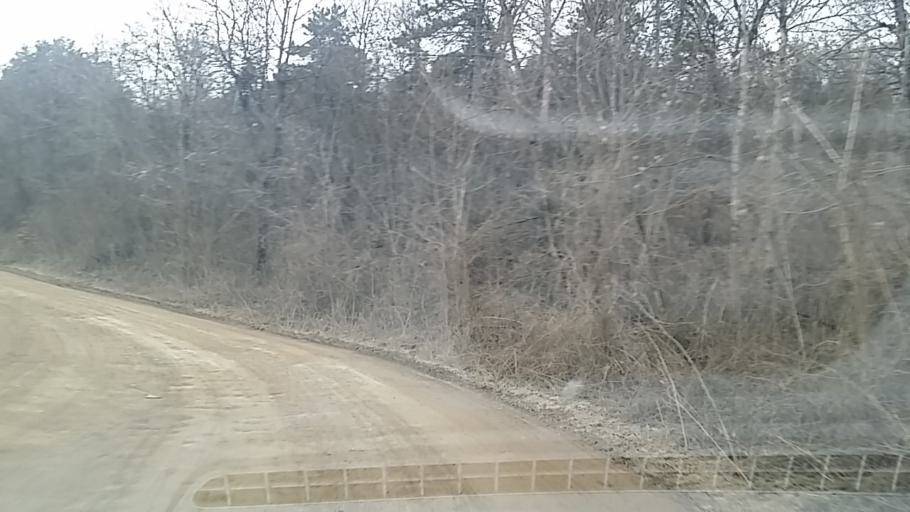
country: HU
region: Borsod-Abauj-Zemplen
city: Rudabanya
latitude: 48.3860
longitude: 20.6367
